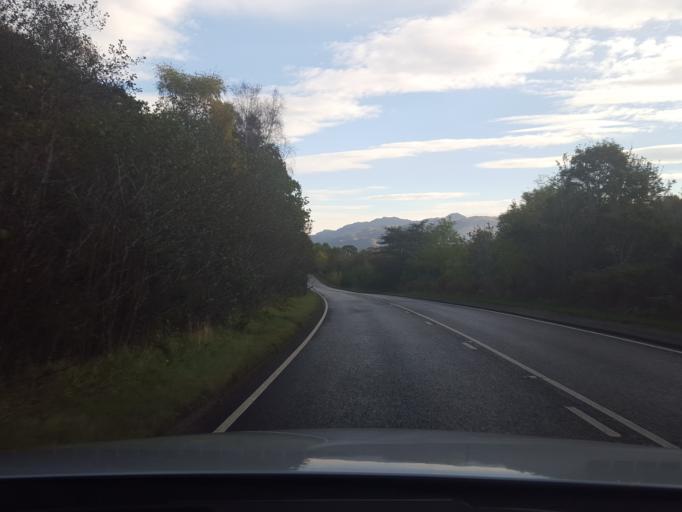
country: GB
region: Scotland
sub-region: Highland
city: Portree
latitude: 57.2851
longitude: -5.5733
